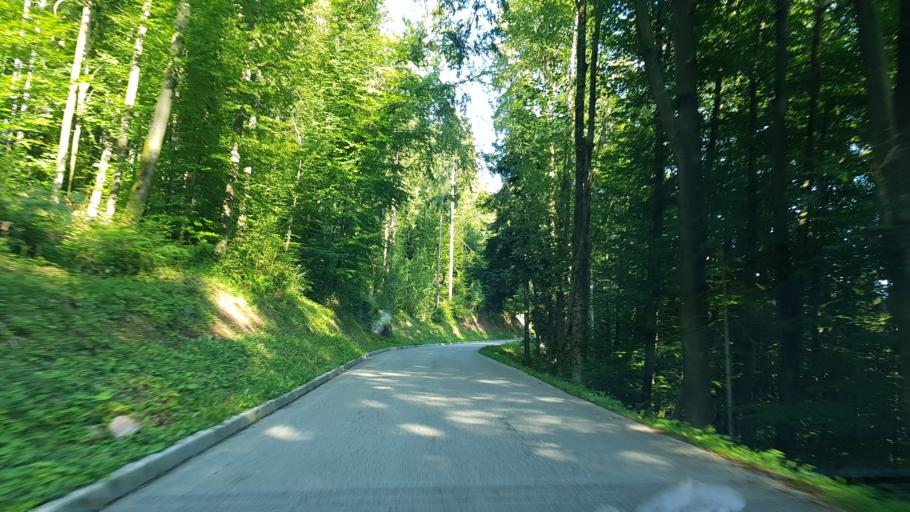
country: SI
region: Idrija
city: Spodnja Idrija
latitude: 46.0744
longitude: 14.0101
